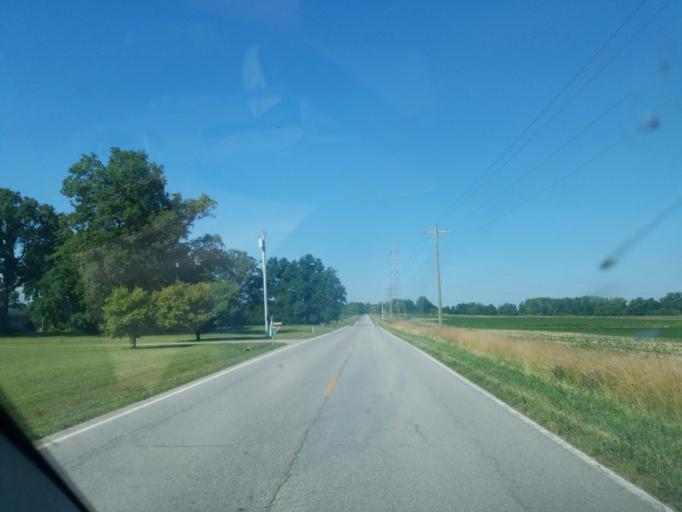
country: US
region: Ohio
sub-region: Union County
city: Richwood
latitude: 40.4183
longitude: -83.4432
